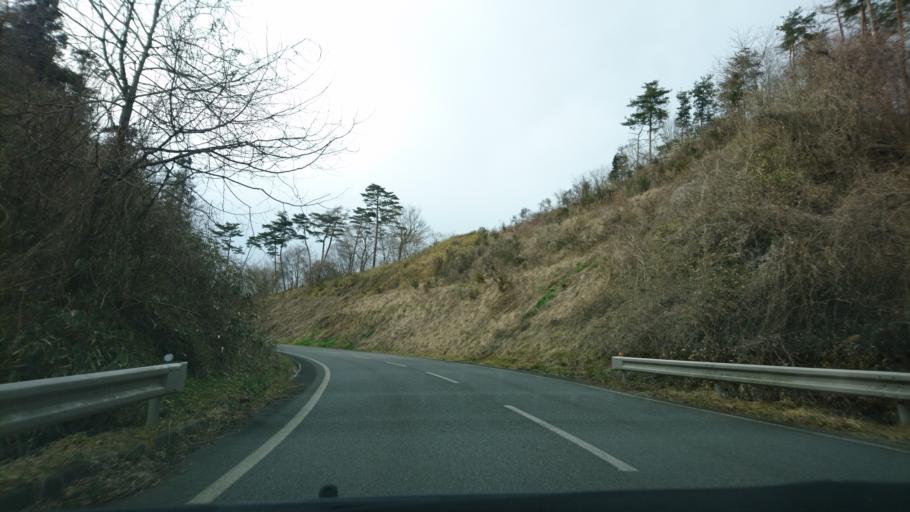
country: JP
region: Iwate
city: Ichinoseki
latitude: 38.8408
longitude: 141.2167
